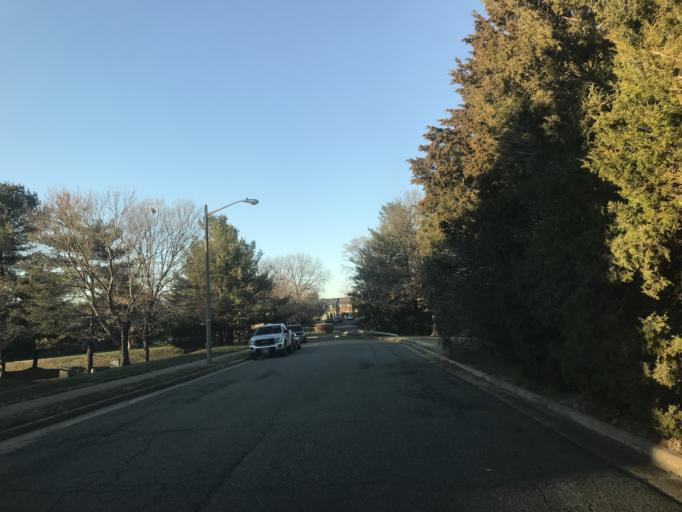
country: US
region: Virginia
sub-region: Fairfax County
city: Franconia
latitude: 38.7747
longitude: -77.1527
